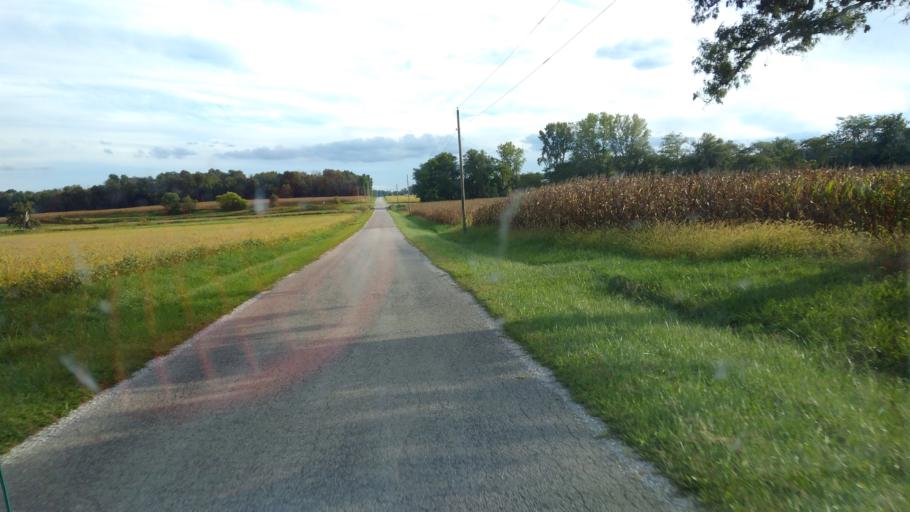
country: US
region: Ohio
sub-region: Crawford County
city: Bucyrus
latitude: 40.8925
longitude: -82.9211
